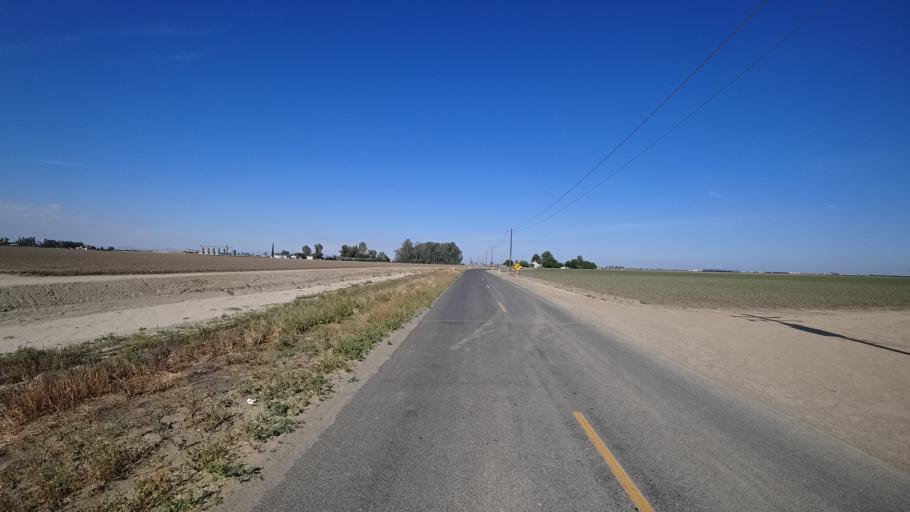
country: US
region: California
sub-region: Kings County
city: Home Garden
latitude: 36.2258
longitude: -119.6324
